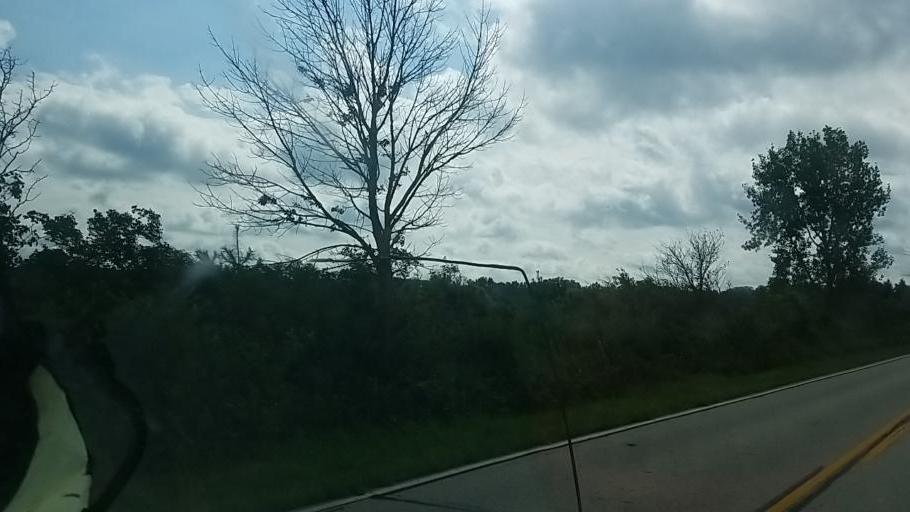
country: US
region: Ohio
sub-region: Pickaway County
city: Commercial Point
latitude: 39.7616
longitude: -83.1583
